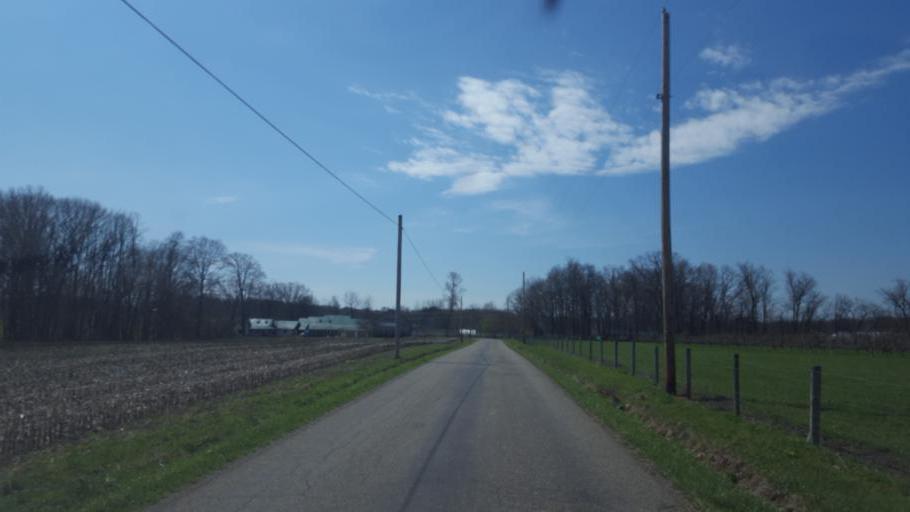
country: US
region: Ohio
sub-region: Knox County
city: Gambier
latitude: 40.3634
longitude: -82.4383
